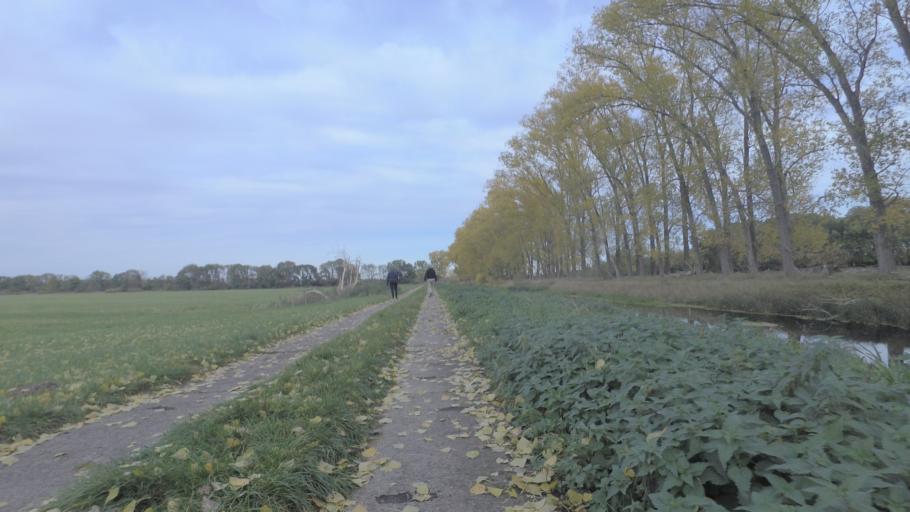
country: DE
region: Brandenburg
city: Ludwigsfelde
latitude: 52.2582
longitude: 13.2832
